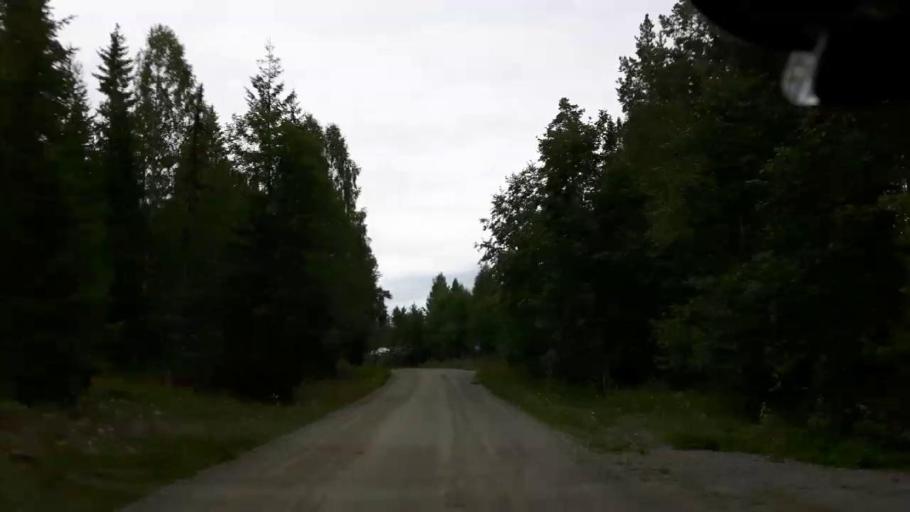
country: SE
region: Jaemtland
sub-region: Braecke Kommun
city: Braecke
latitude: 62.8313
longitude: 15.6897
